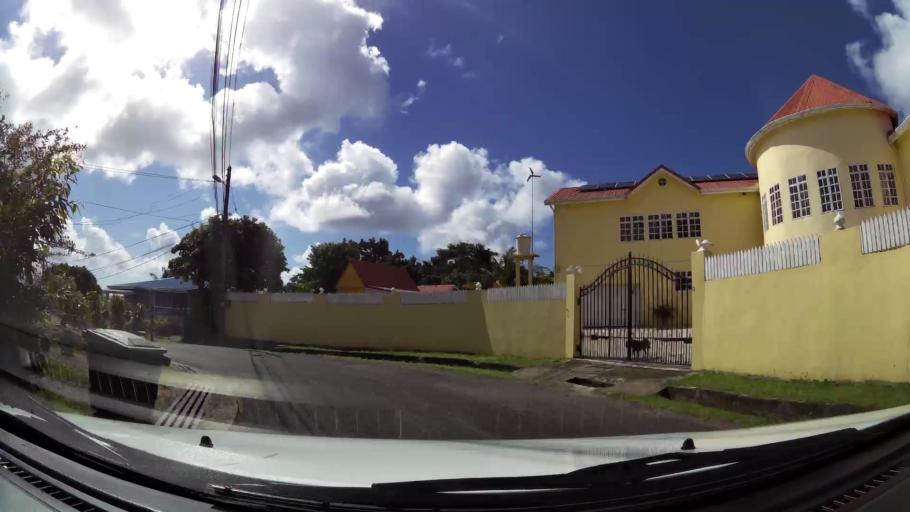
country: LC
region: Castries Quarter
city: Castries
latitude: 13.9996
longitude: -60.9999
